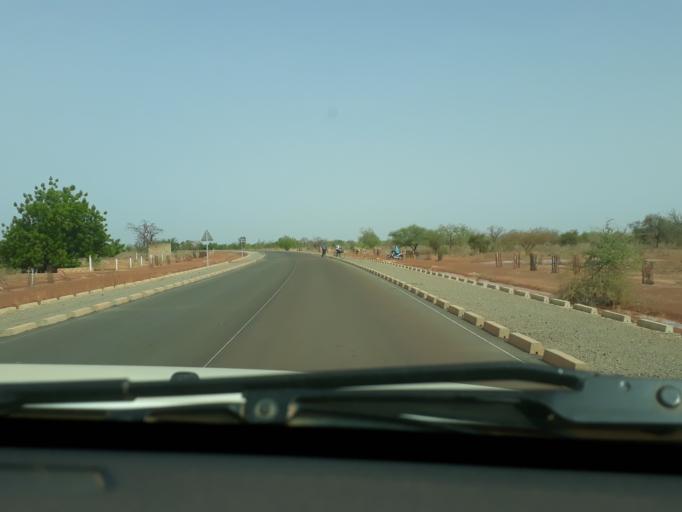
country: BF
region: Plateau-Central
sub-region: Province d'Oubritenga
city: Ziniare
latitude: 12.5498
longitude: -1.3915
